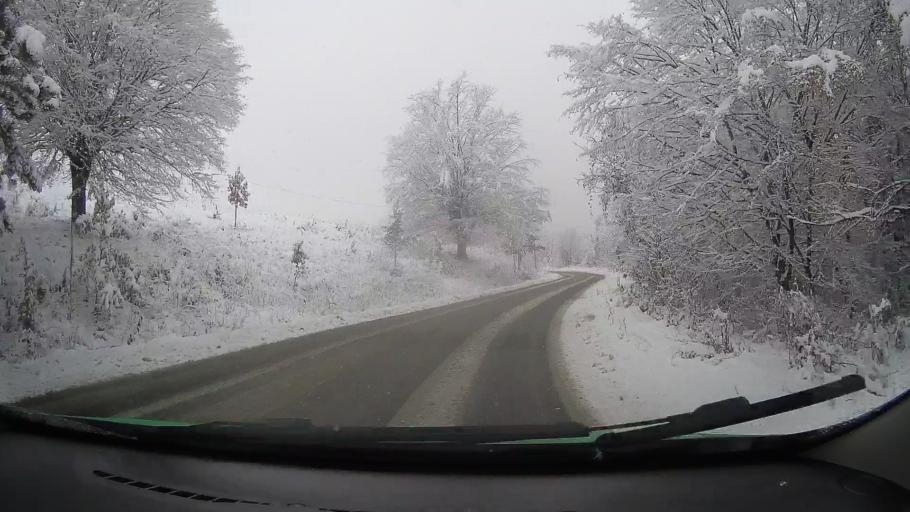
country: RO
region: Hunedoara
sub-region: Comuna Teliucu Inferior
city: Teliucu Inferior
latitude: 45.7051
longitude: 22.8820
